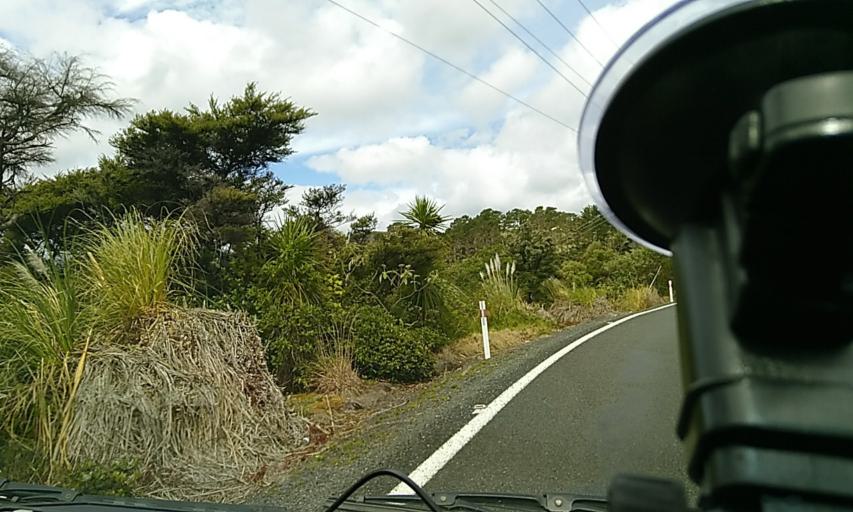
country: NZ
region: Northland
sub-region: Far North District
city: Ahipara
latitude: -35.5381
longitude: 173.3846
